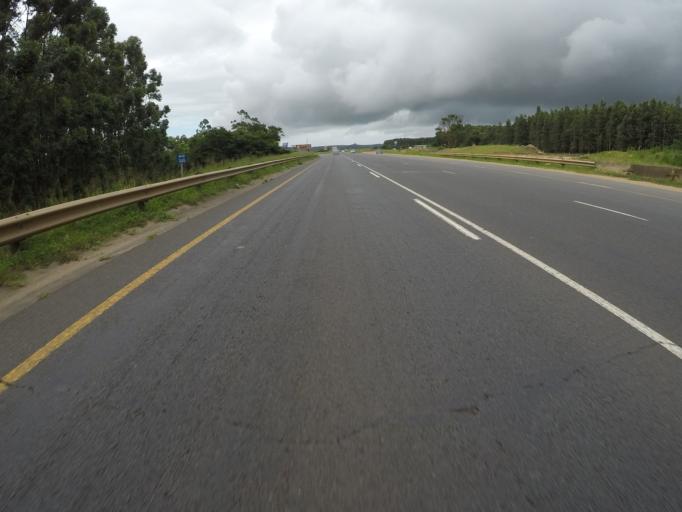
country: ZA
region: KwaZulu-Natal
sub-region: uThungulu District Municipality
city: Empangeni
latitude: -28.8100
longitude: 31.9158
